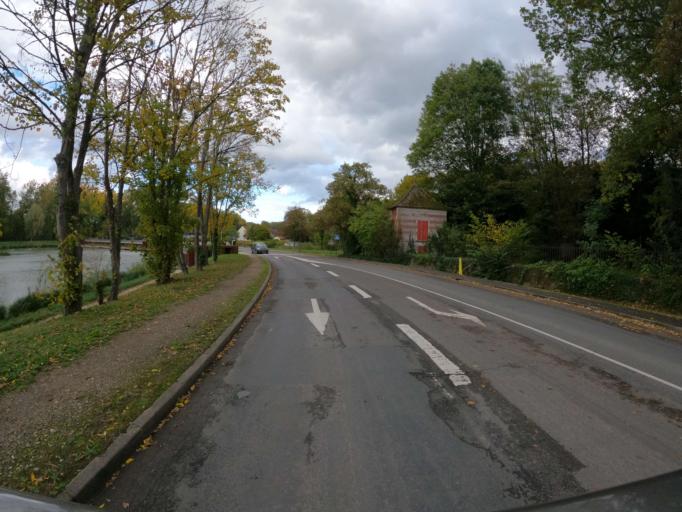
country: FR
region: Ile-de-France
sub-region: Departement de Seine-et-Marne
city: Coupvray
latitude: 48.8953
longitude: 2.7957
